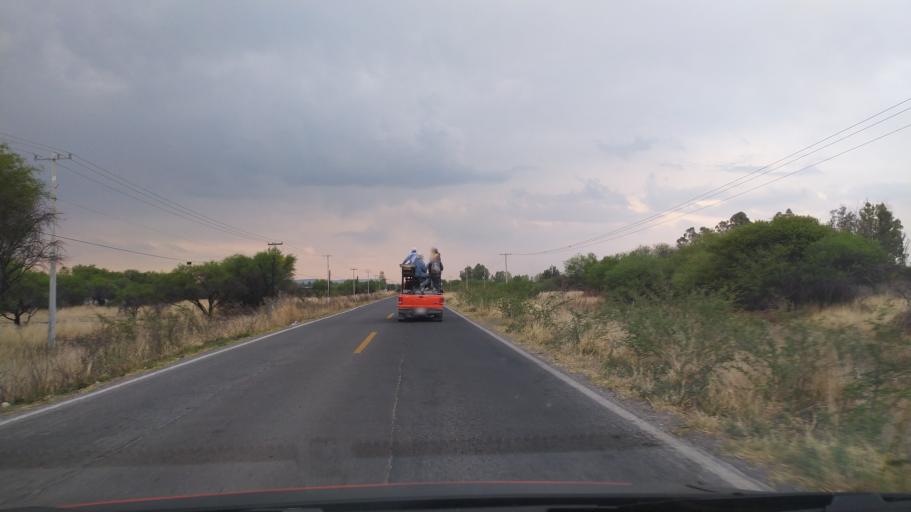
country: MX
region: Guanajuato
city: Ciudad Manuel Doblado
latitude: 20.8027
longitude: -101.9054
